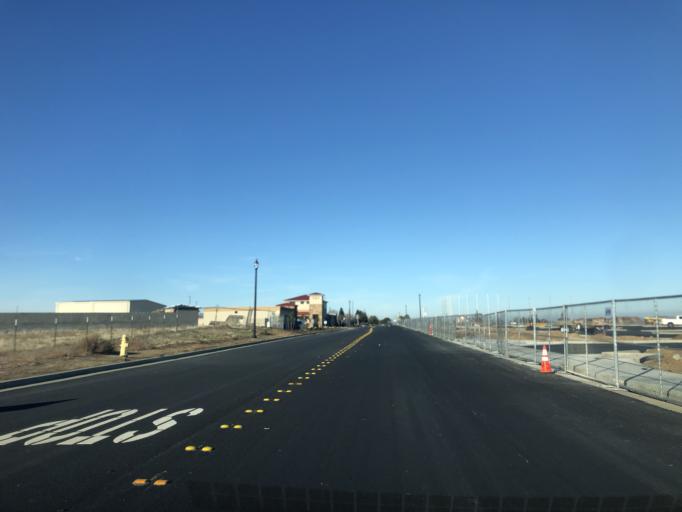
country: US
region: California
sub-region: Sacramento County
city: Antelope
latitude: 38.7821
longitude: -121.3771
